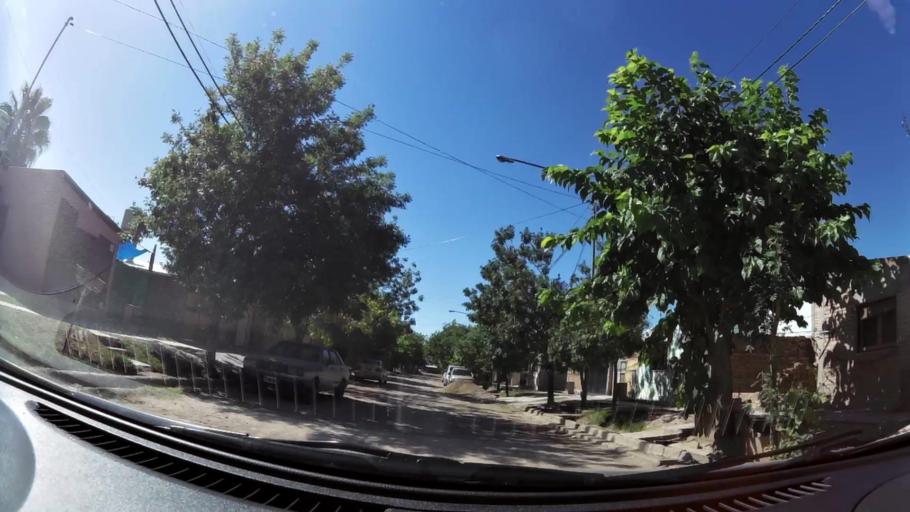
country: AR
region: Mendoza
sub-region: Departamento de Godoy Cruz
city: Godoy Cruz
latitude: -32.9615
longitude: -68.8353
